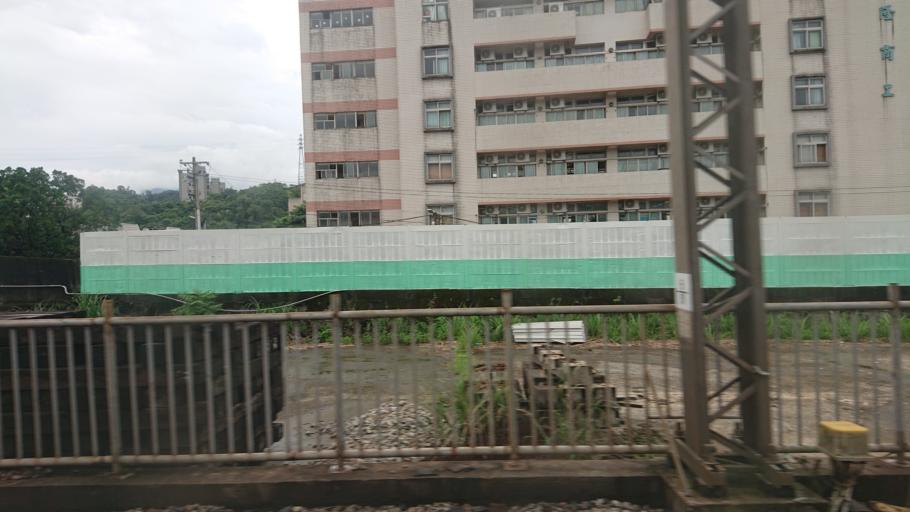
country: TW
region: Taiwan
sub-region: Keelung
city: Keelung
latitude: 25.0952
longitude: 121.7172
